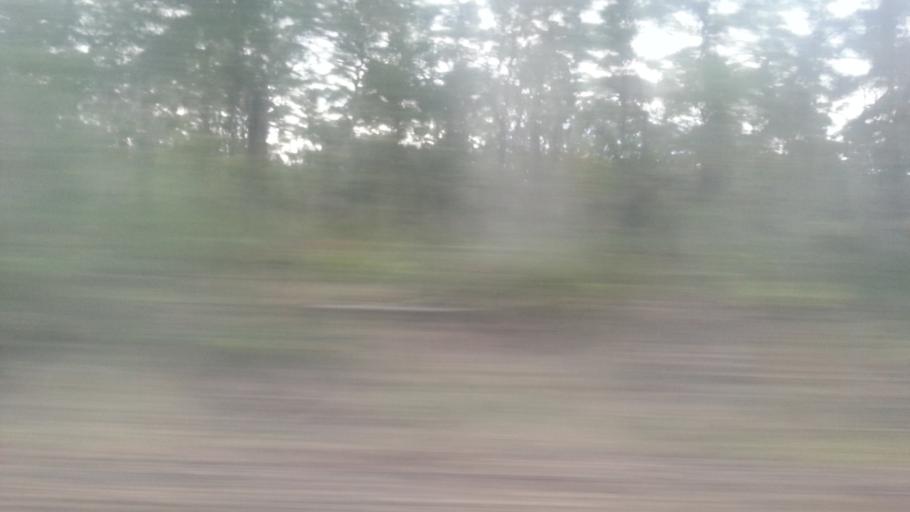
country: AU
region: New South Wales
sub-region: Wollongong
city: Mount Ousley
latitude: -34.3900
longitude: 150.8496
